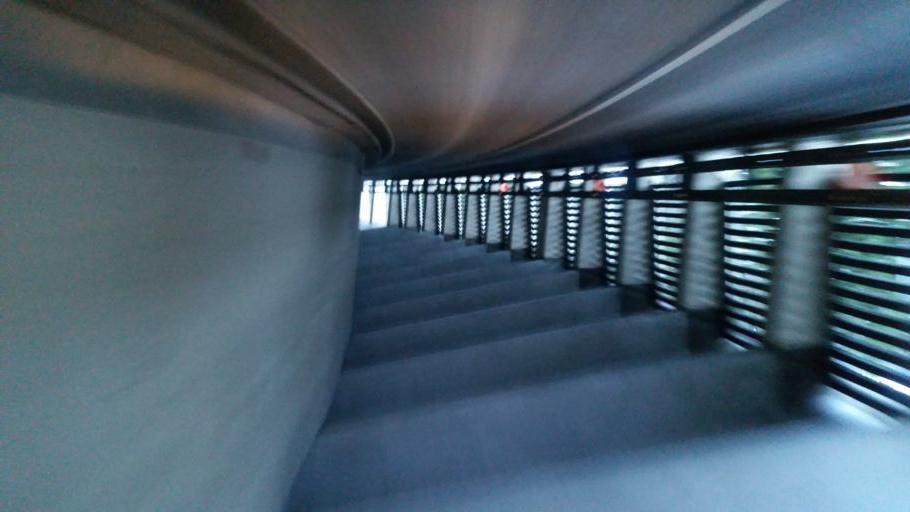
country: AT
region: Salzburg
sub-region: Politischer Bezirk Sankt Johann im Pongau
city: Untertauern
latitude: 47.2634
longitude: 13.5001
